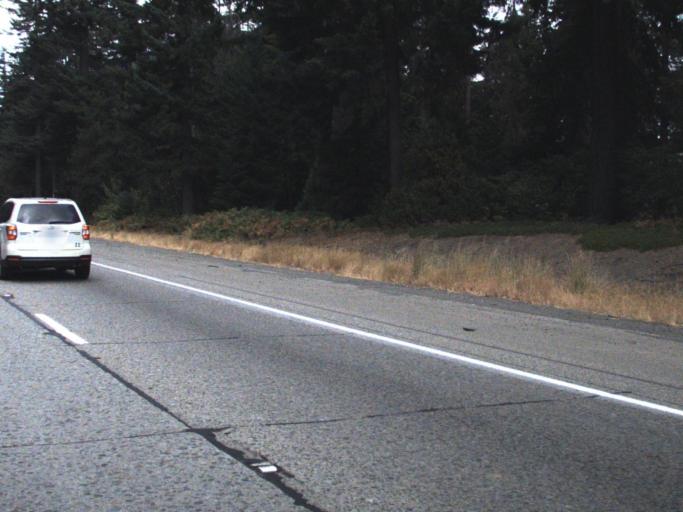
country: US
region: Washington
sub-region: Kittitas County
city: Cle Elum
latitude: 47.2644
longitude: -121.2181
